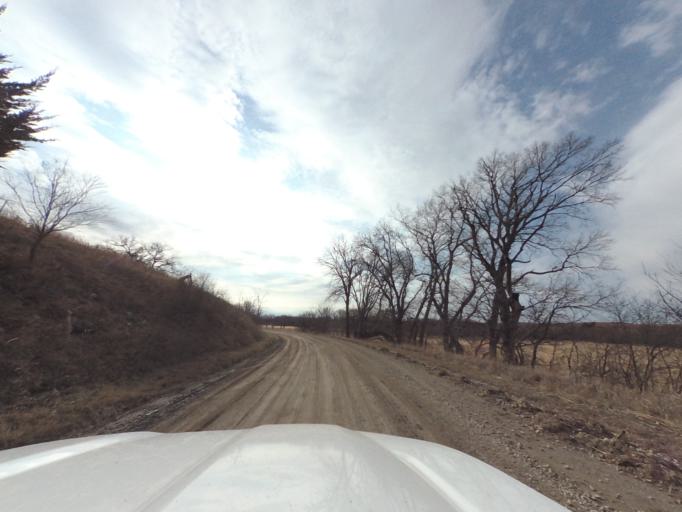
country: US
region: Kansas
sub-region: Chase County
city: Cottonwood Falls
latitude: 38.2812
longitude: -96.7350
